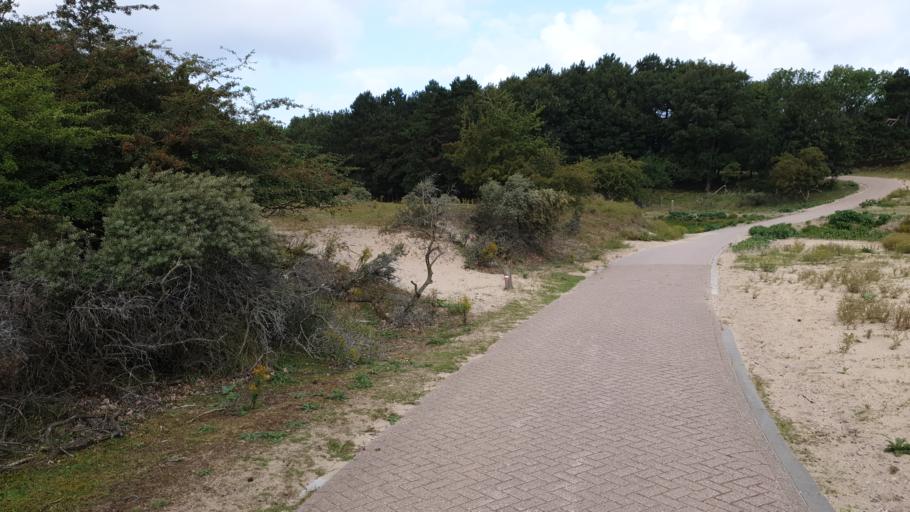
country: NL
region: South Holland
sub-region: Gemeente Lisse
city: Lisse
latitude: 52.3041
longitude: 4.5262
